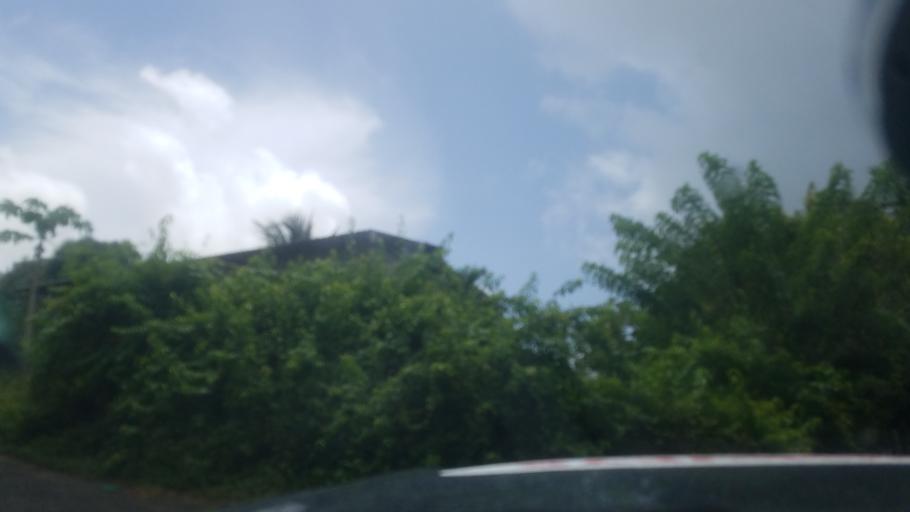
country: LC
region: Laborie Quarter
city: Laborie
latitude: 13.7468
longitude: -60.9630
